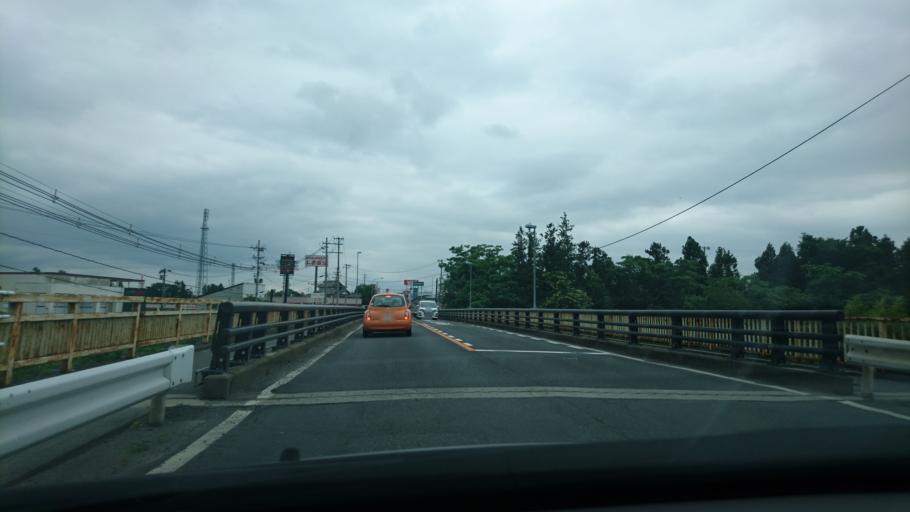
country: JP
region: Miyagi
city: Furukawa
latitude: 38.7414
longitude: 141.0180
